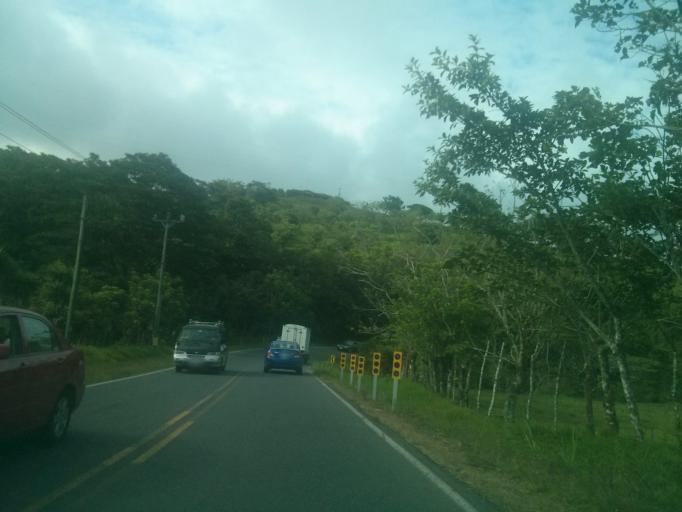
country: CR
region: Cartago
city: Paraiso
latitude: 9.8601
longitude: -83.8404
